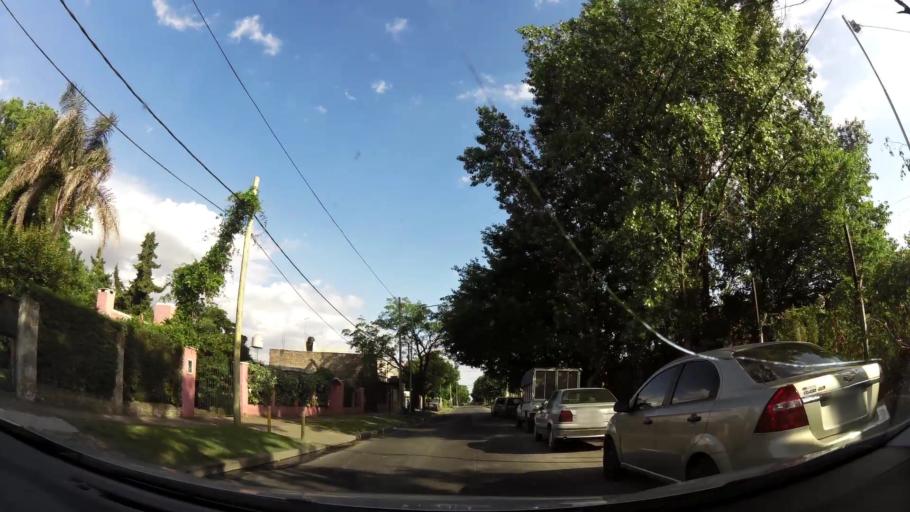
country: AR
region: Buenos Aires
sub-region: Partido de Tigre
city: Tigre
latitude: -34.4732
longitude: -58.6551
